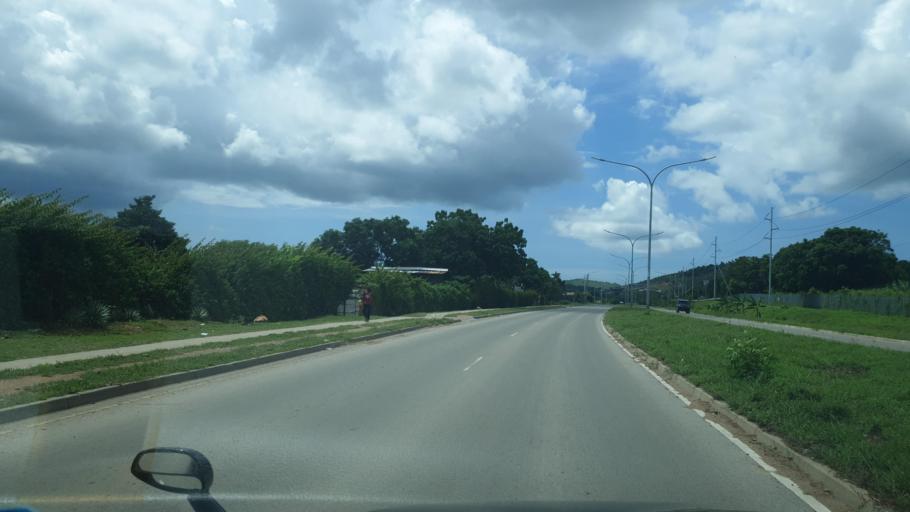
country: PG
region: National Capital
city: Port Moresby
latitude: -9.3826
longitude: 147.1556
